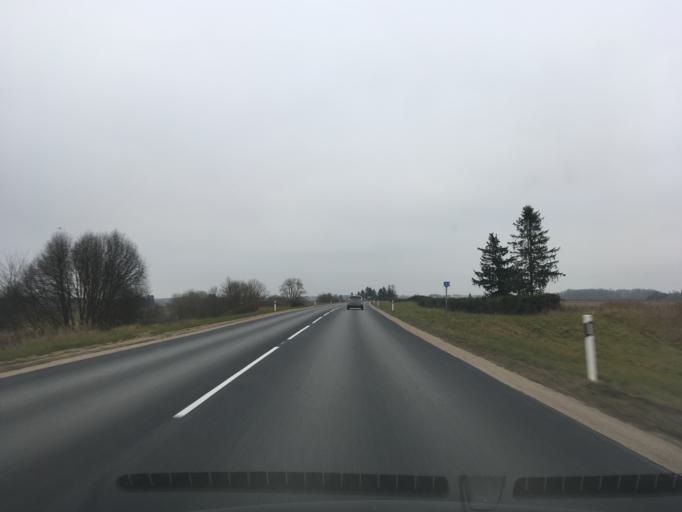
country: EE
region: Ida-Virumaa
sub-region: Aseri vald
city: Aseri
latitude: 59.4441
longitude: 26.7808
